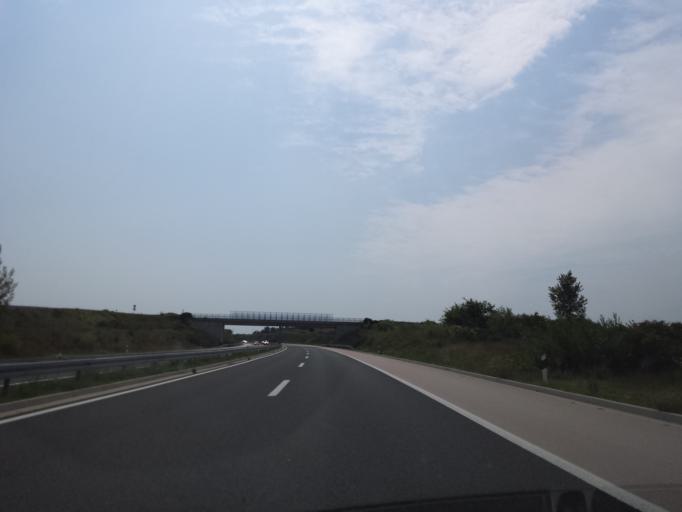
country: HR
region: Zadarska
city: Policnik
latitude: 44.1637
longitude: 15.4193
